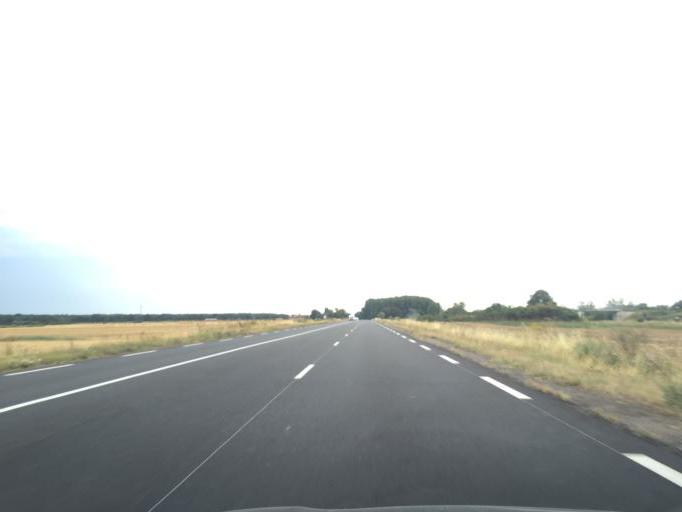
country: FR
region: Auvergne
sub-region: Departement de l'Allier
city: Bessay-sur-Allier
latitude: 46.4171
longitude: 3.3540
